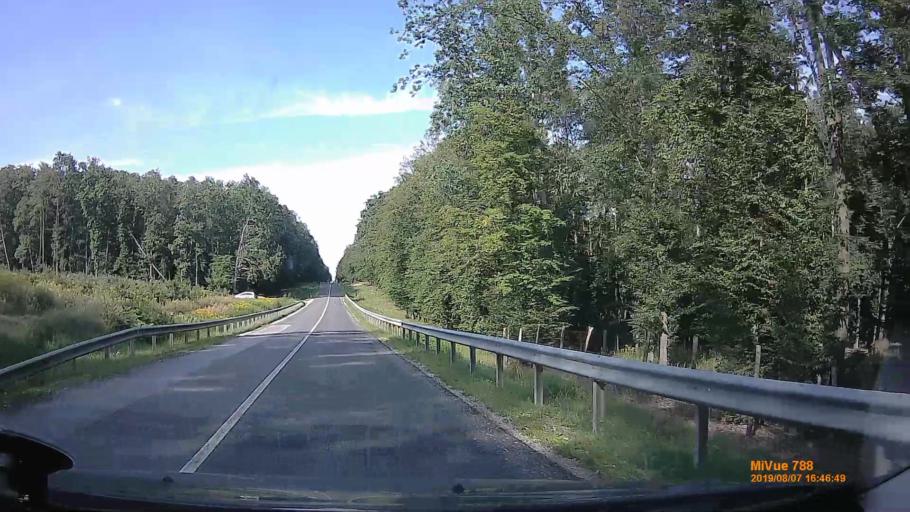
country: HU
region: Zala
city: Lenti
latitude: 46.6560
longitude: 16.6292
